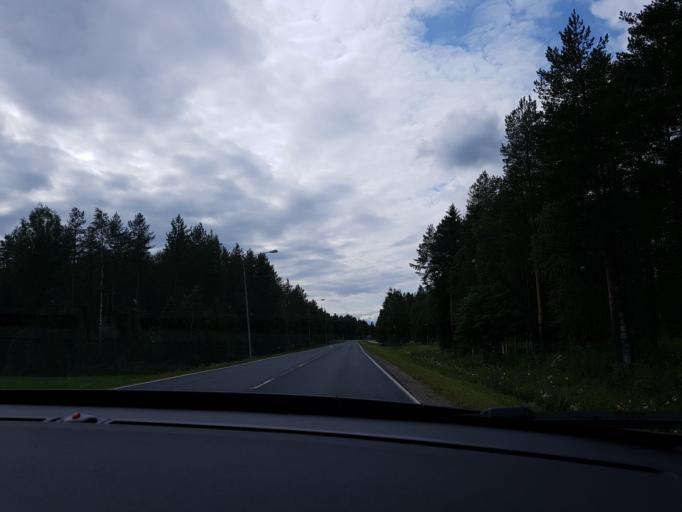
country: FI
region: Kainuu
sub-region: Kehys-Kainuu
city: Kuhmo
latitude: 64.1178
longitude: 29.5356
